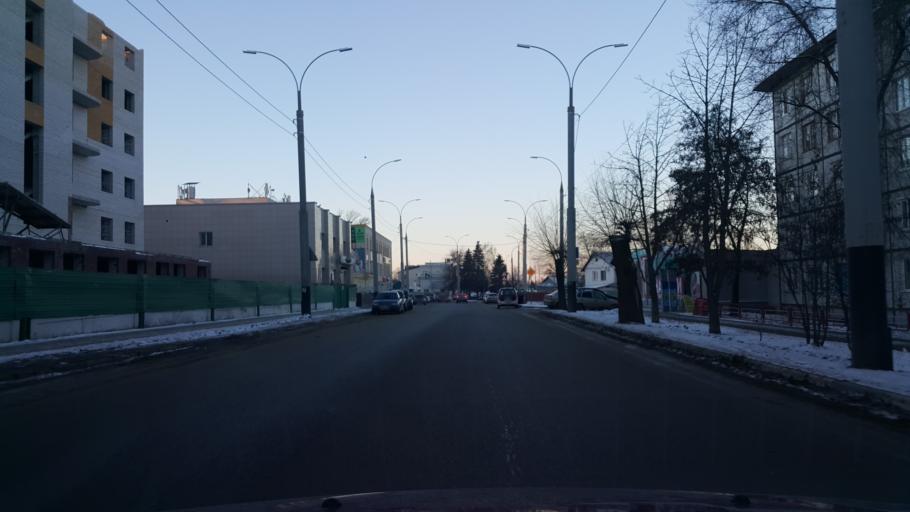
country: RU
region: Tambov
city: Pokrovo-Prigorodnoye
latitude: 52.7083
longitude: 41.3974
